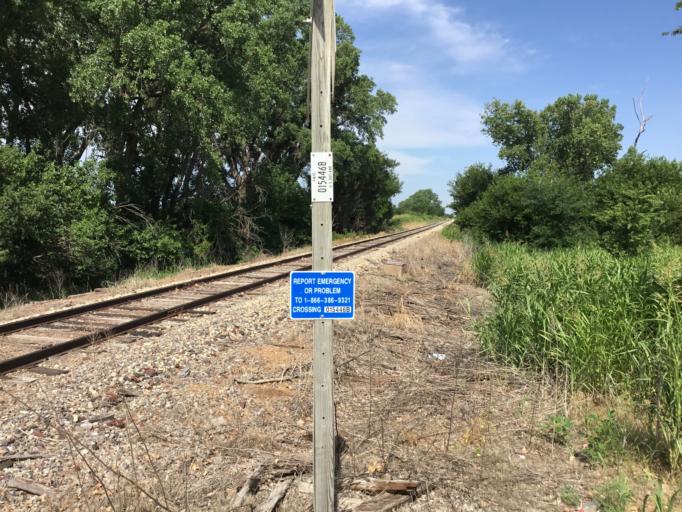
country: US
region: Kansas
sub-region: Kingman County
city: Kingman
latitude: 37.4431
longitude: -98.2455
